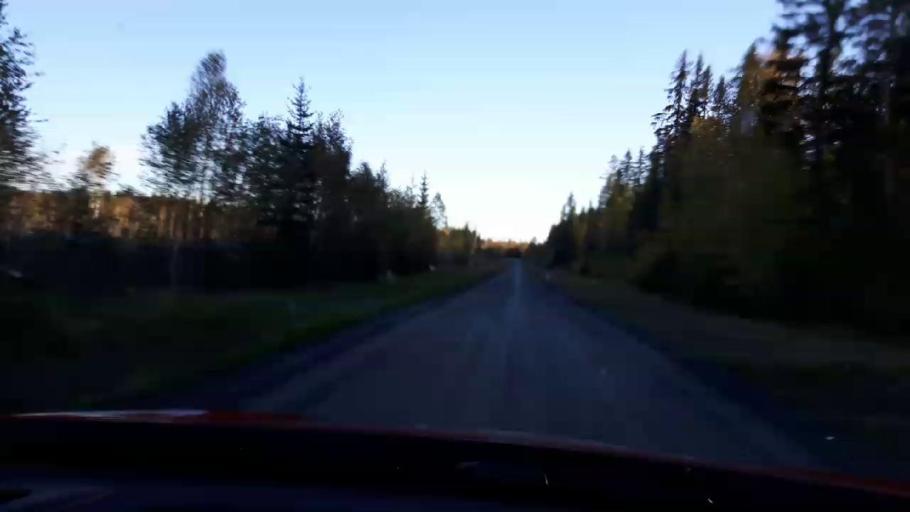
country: SE
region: Jaemtland
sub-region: OEstersunds Kommun
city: Lit
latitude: 63.6589
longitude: 14.7151
